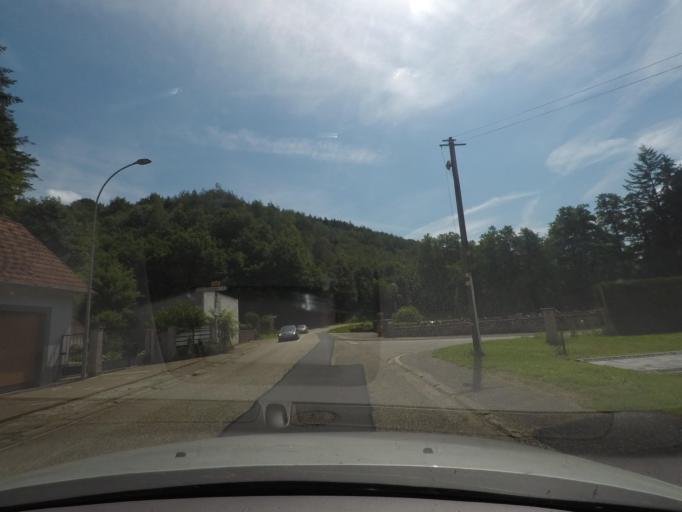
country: FR
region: Lorraine
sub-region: Departement de la Moselle
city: Phalsbourg
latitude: 48.8166
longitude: 7.2844
